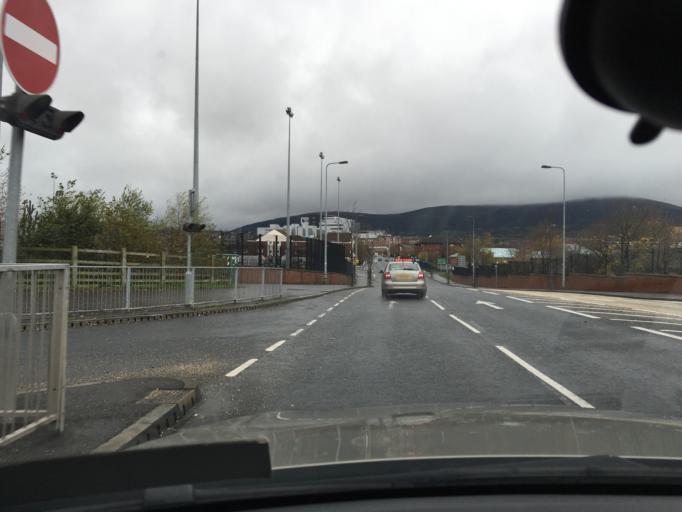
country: GB
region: Northern Ireland
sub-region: City of Belfast
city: Belfast
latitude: 54.5955
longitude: -5.9431
